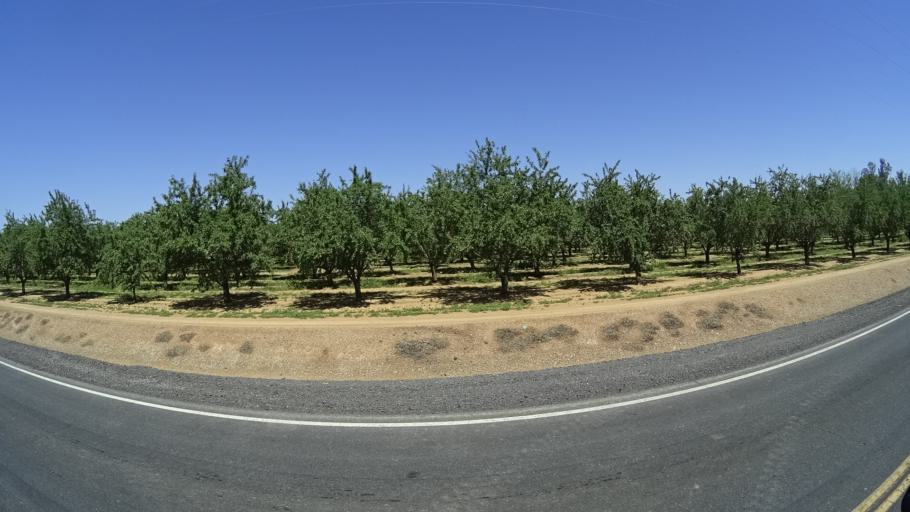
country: US
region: California
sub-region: Glenn County
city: Hamilton City
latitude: 39.7665
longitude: -122.0866
